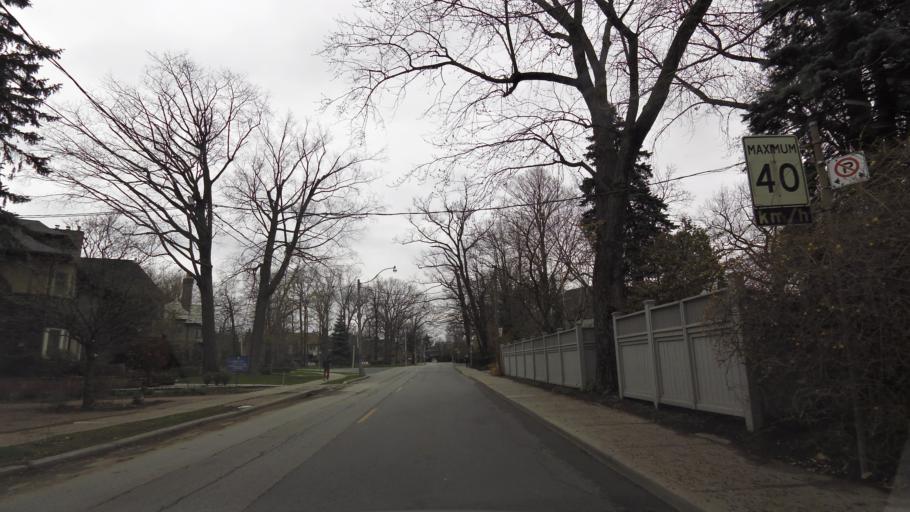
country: CA
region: Ontario
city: Toronto
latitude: 43.6825
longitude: -79.3733
